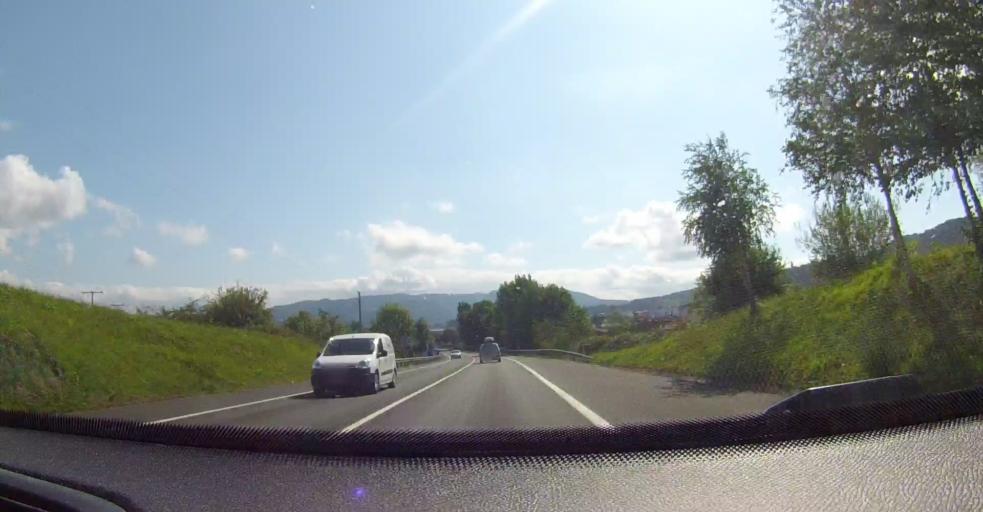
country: ES
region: Basque Country
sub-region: Bizkaia
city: Gernika-Lumo
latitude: 43.3160
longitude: -2.6696
